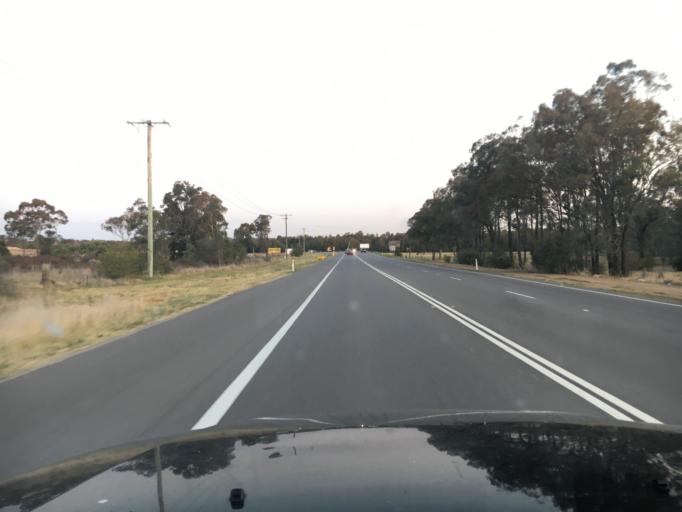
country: AU
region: New South Wales
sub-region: Cessnock
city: Greta
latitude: -32.6685
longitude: 151.3764
